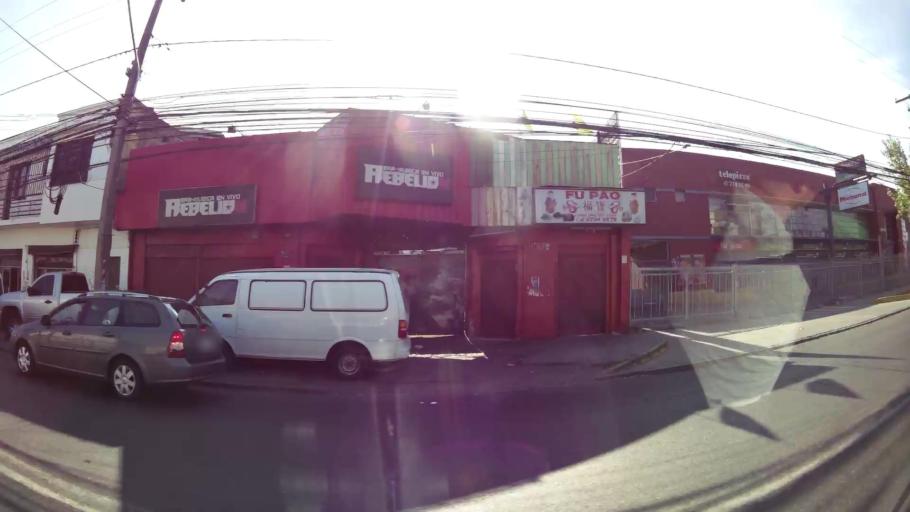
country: CL
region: Santiago Metropolitan
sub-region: Provincia de Santiago
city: Santiago
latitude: -33.3952
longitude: -70.6724
